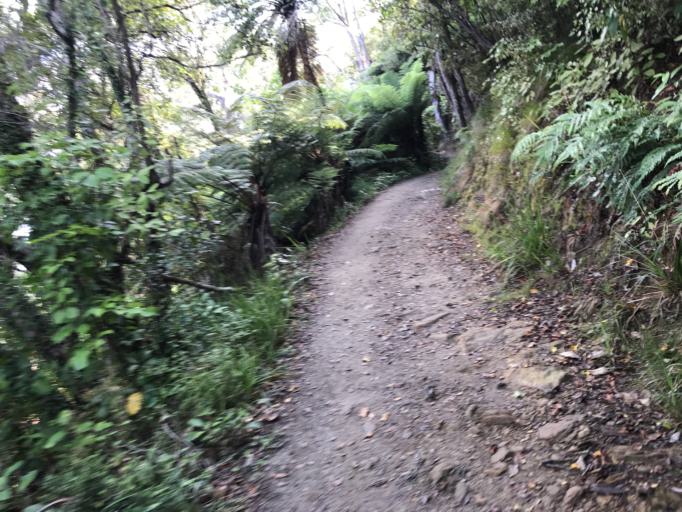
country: NZ
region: Marlborough
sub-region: Marlborough District
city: Picton
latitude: -41.2625
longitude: 173.9287
